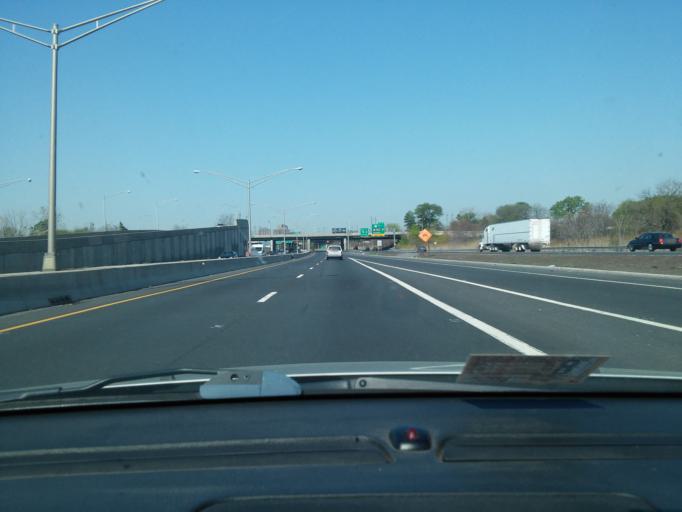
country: US
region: New Jersey
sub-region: Essex County
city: Newark
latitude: 40.7111
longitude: -74.1744
